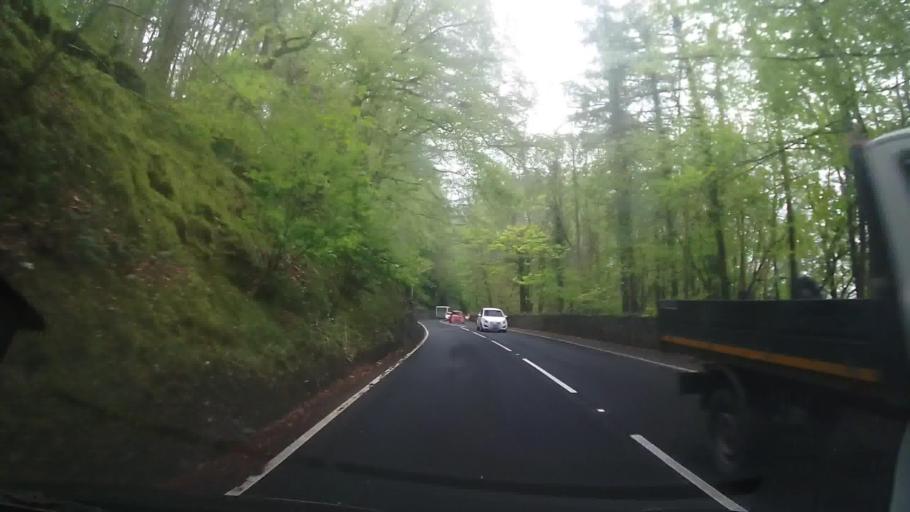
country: GB
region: Wales
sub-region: Denbighshire
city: Llangollen
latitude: 52.9808
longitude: -3.2034
